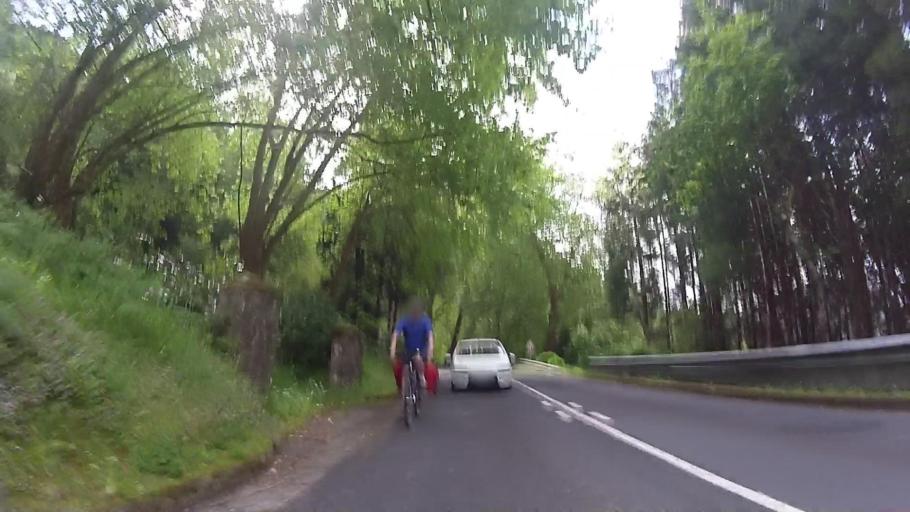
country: PT
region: Azores
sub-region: Povoacao
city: Furnas
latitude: 37.7676
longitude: -25.2897
